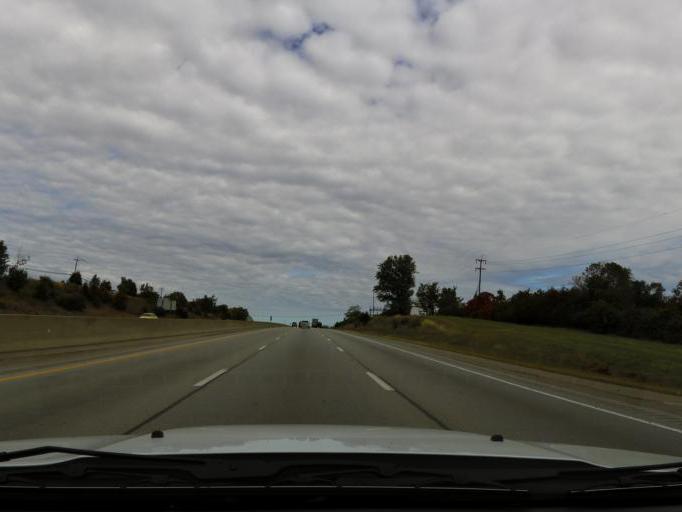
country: US
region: Kentucky
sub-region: Boone County
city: Walton
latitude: 38.8665
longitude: -84.6237
